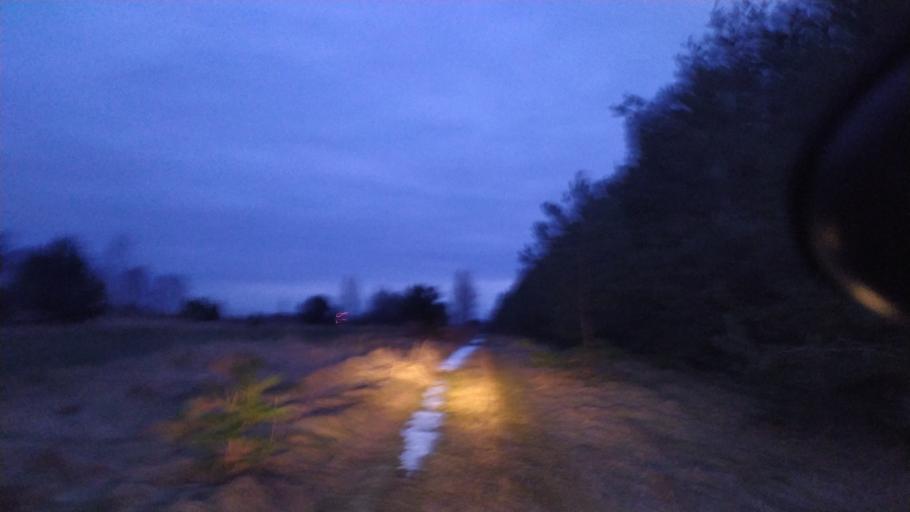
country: PL
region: Lublin Voivodeship
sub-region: Powiat lubelski
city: Jastkow
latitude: 51.3845
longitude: 22.4368
